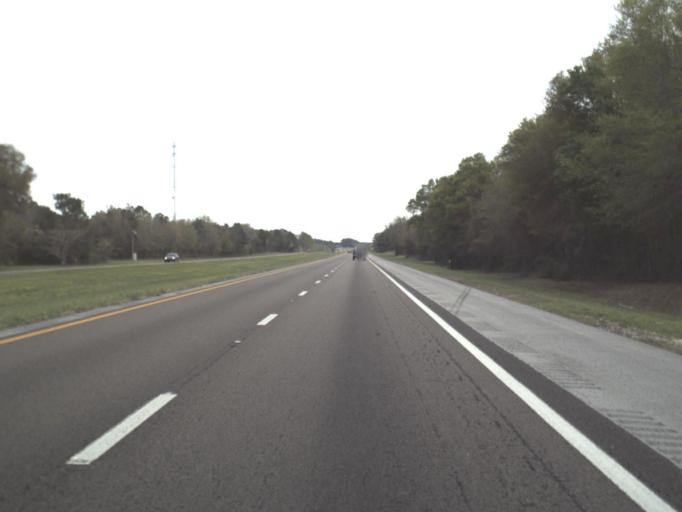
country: US
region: Florida
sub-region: Walton County
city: DeFuniak Springs
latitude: 30.7420
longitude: -86.2292
